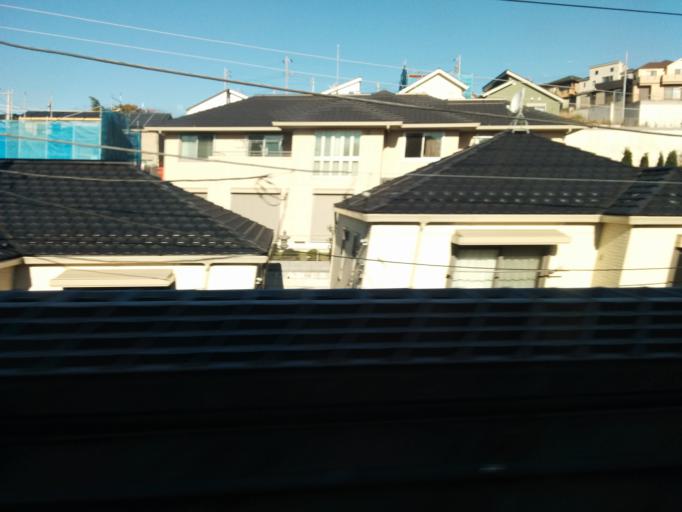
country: JP
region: Kanagawa
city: Yokohama
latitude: 35.4889
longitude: 139.5952
